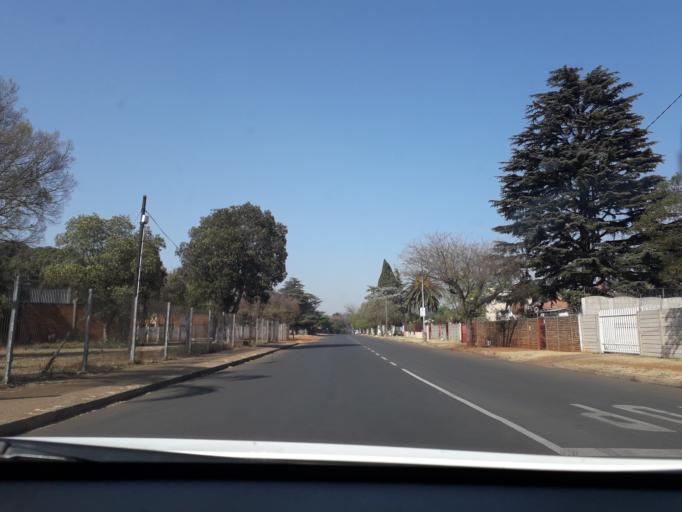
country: ZA
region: Gauteng
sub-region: City of Johannesburg Metropolitan Municipality
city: Modderfontein
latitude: -26.0975
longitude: 28.2409
